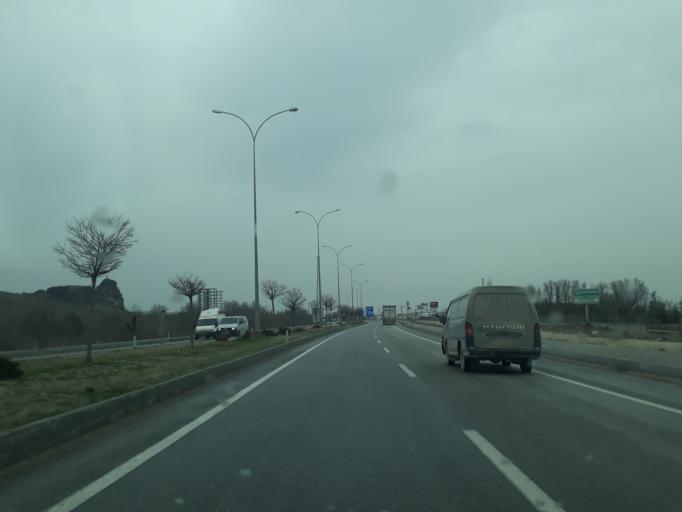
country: TR
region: Konya
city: Karapinar
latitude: 37.7152
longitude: 33.5799
